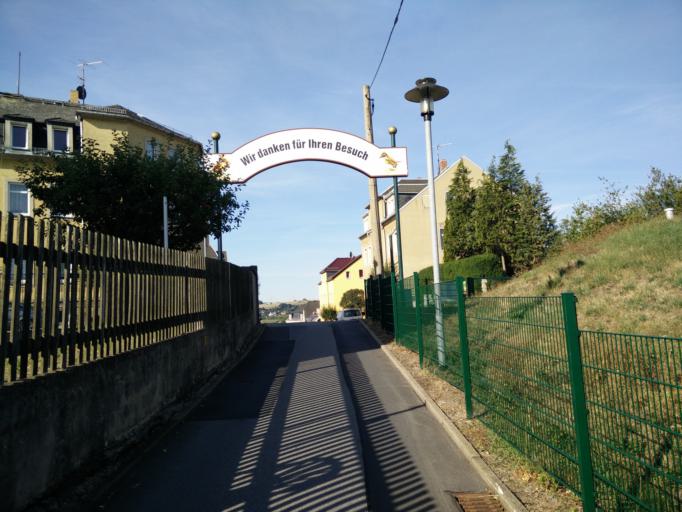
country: DE
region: Saxony
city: Rabenau
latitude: 50.9668
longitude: 13.6429
